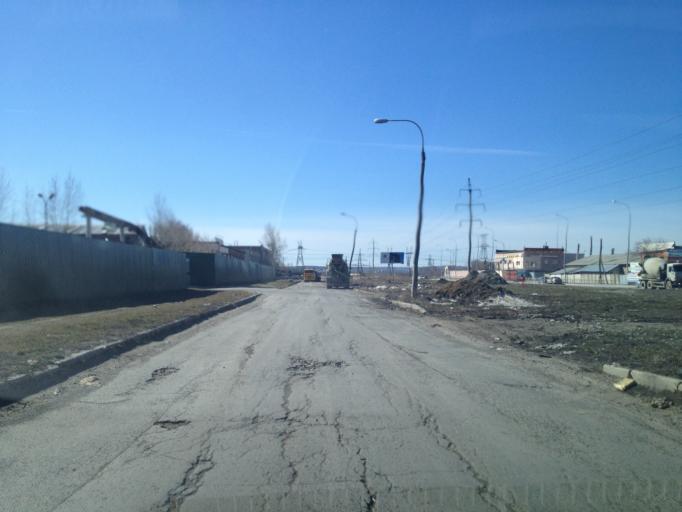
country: RU
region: Sverdlovsk
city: Sovkhoznyy
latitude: 56.7560
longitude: 60.5871
